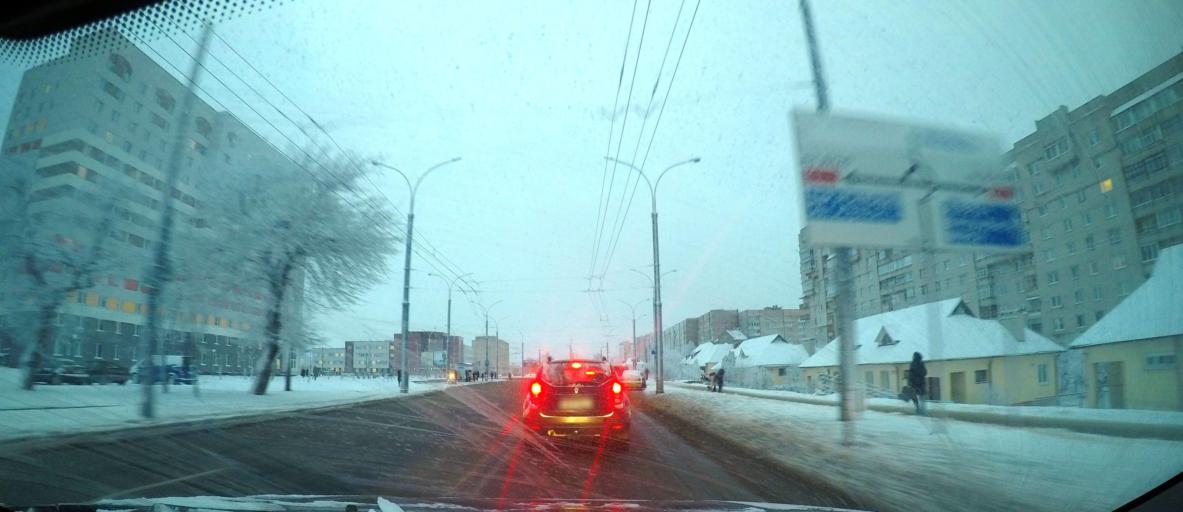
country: BY
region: Grodnenskaya
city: Hrodna
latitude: 53.6996
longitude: 23.8399
